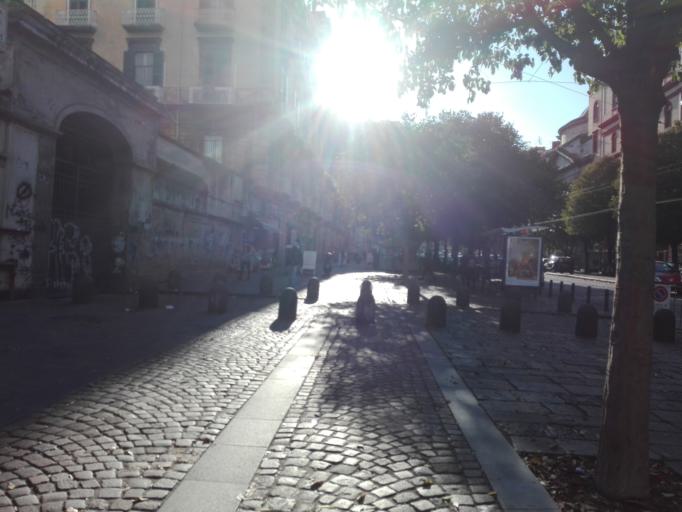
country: IT
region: Campania
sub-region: Provincia di Napoli
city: Napoli
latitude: 40.8571
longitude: 14.2593
